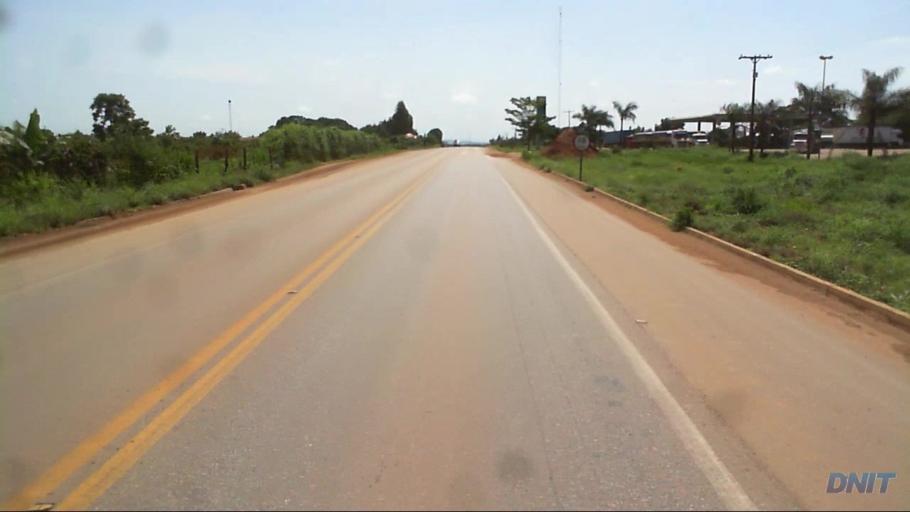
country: BR
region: Goias
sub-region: Barro Alto
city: Barro Alto
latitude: -15.2080
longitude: -48.7046
